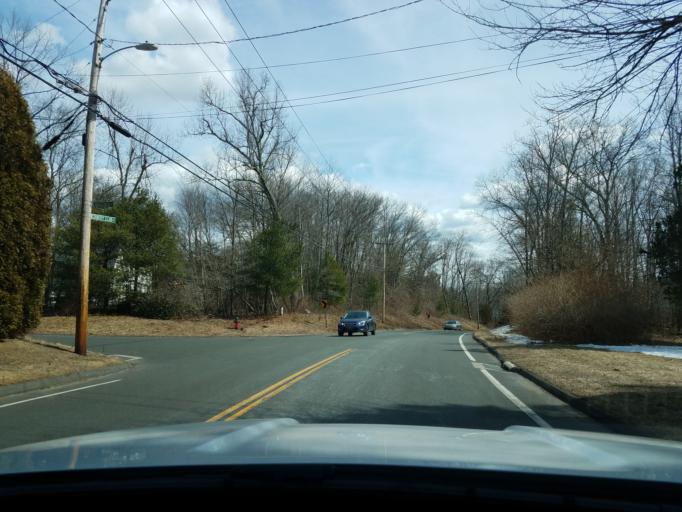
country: US
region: Connecticut
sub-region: Hartford County
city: Canton Valley
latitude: 41.7906
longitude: -72.8738
